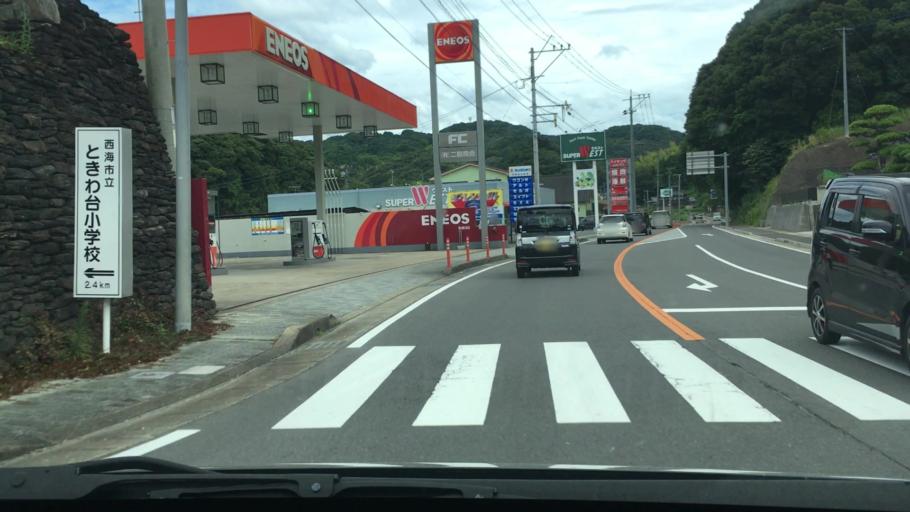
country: JP
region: Nagasaki
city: Togitsu
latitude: 32.9856
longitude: 129.7776
